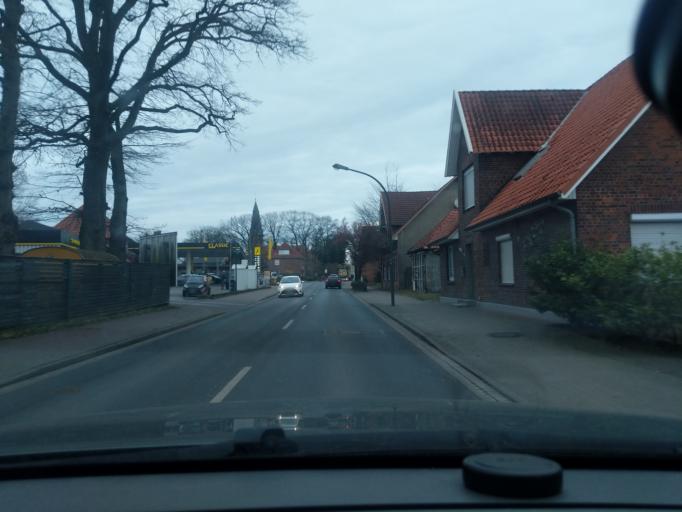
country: DE
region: Lower Saxony
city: Apensen
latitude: 53.4322
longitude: 9.6138
